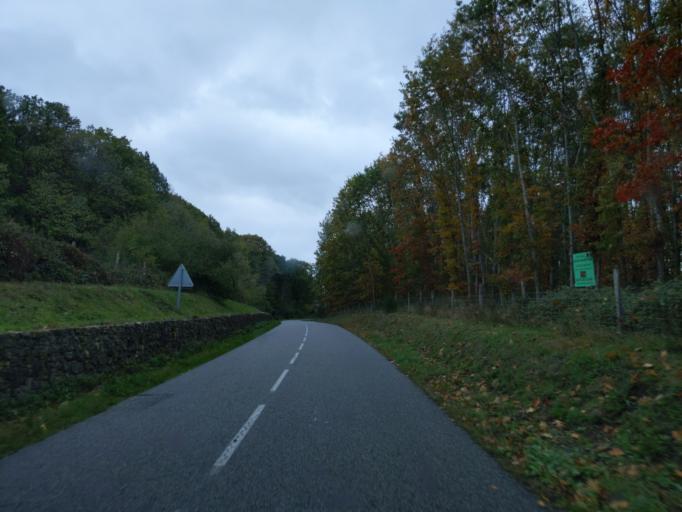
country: FR
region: Ile-de-France
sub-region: Departement des Yvelines
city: Bullion
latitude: 48.6280
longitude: 1.9680
